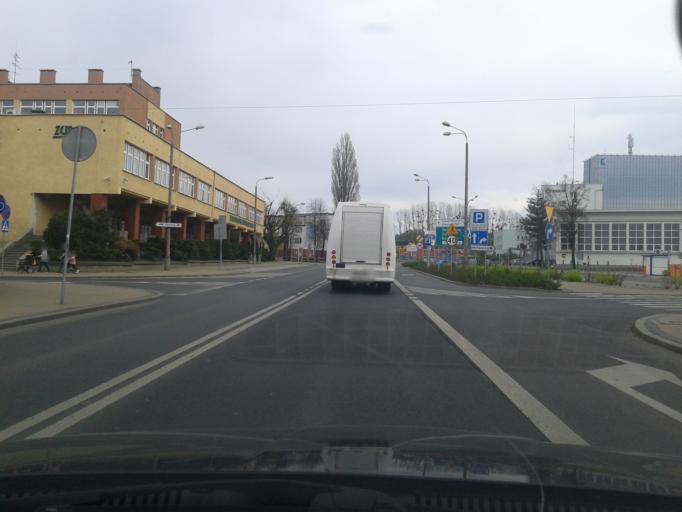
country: PL
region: Silesian Voivodeship
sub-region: Rybnik
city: Rybnik
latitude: 50.0890
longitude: 18.5398
